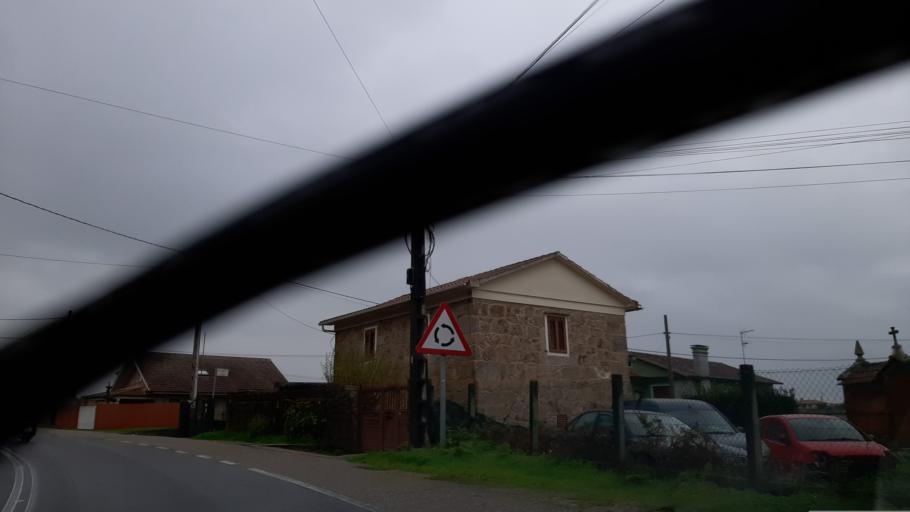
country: ES
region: Galicia
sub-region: Provincia de Pontevedra
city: Nigran
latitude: 42.1696
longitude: -8.8010
